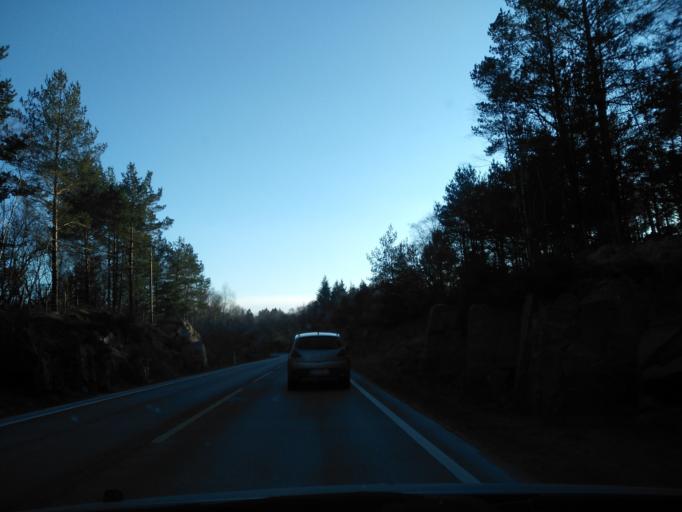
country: NO
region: Rogaland
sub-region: Tysvaer
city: Aksdal
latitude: 59.3846
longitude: 5.4614
